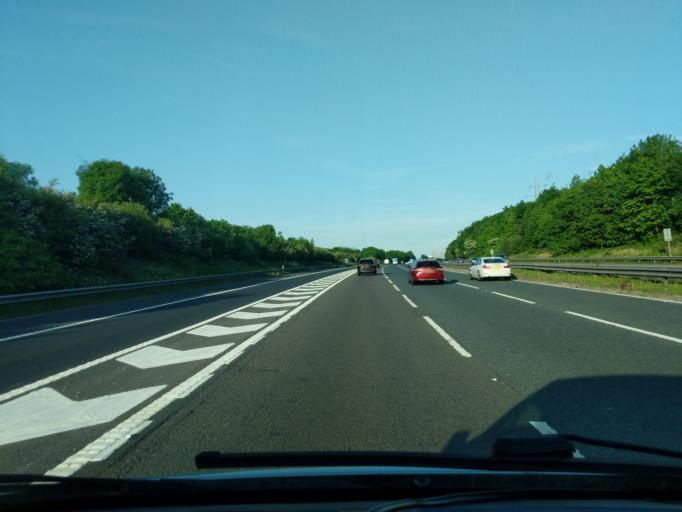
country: GB
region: England
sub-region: Knowsley
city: Whiston
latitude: 53.4015
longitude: -2.7934
